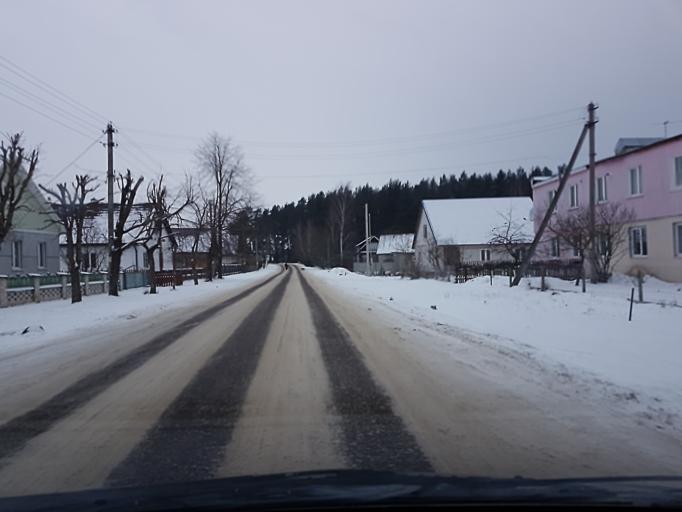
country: BY
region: Minsk
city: Rakaw
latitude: 53.9577
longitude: 27.0603
